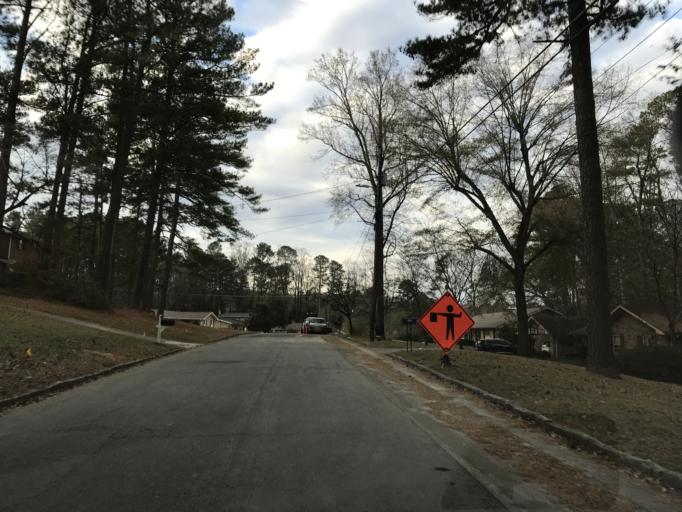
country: US
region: Georgia
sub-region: DeKalb County
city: Doraville
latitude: 33.8802
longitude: -84.2527
